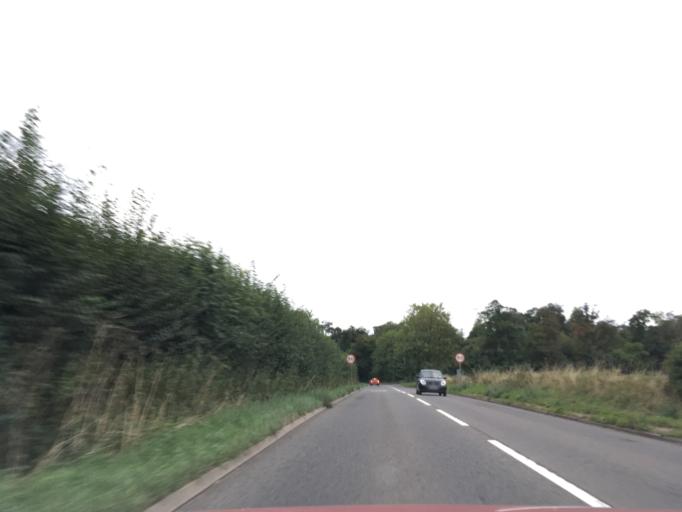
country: GB
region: England
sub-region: Wiltshire
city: Calne
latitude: 51.4013
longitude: -2.0469
